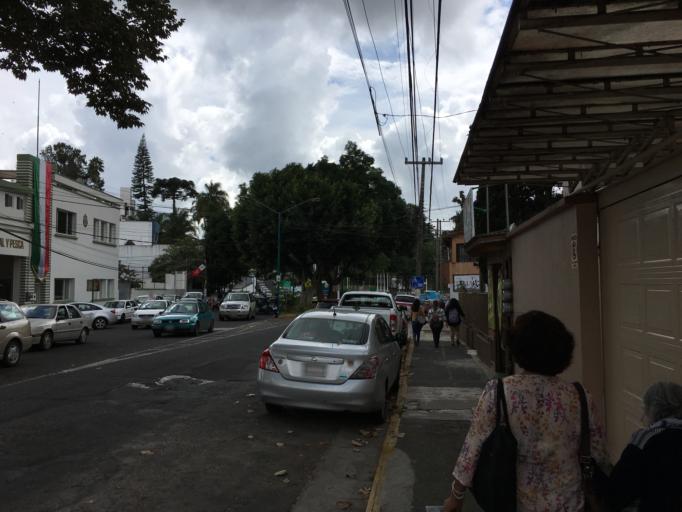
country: MX
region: Veracruz
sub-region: Xalapa
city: Xalapa de Enriquez
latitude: 19.5220
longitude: -96.9176
